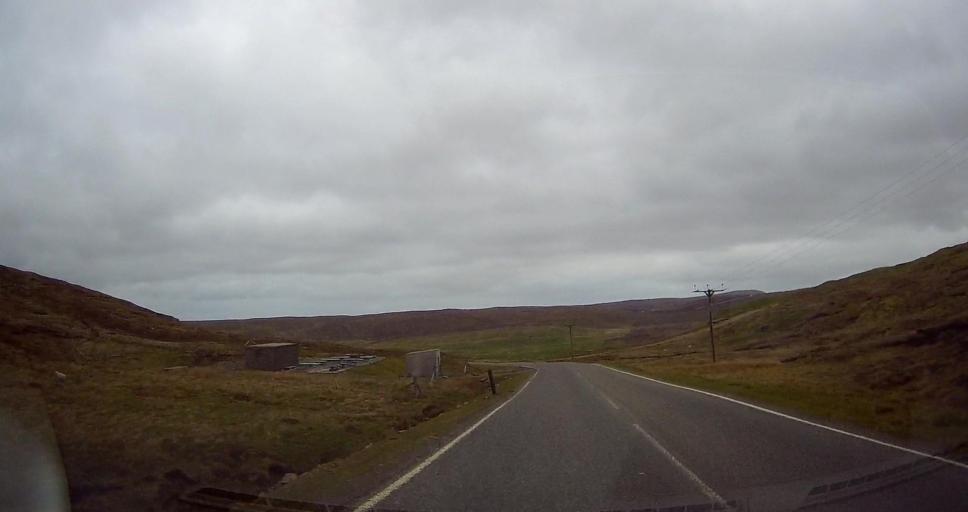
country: GB
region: Scotland
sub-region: Shetland Islands
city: Lerwick
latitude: 60.3429
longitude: -1.2948
